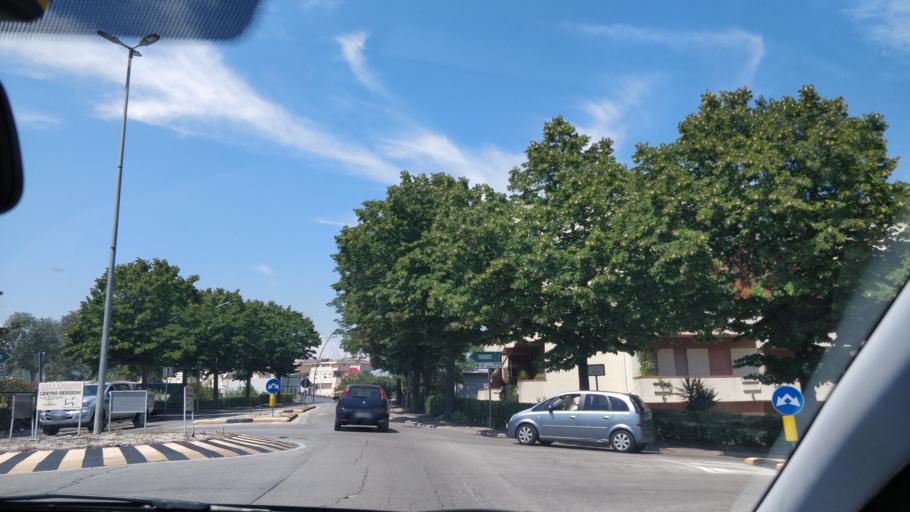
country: IT
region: Abruzzo
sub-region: Provincia di Chieti
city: Francavilla al Mare
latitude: 42.4236
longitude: 14.2802
